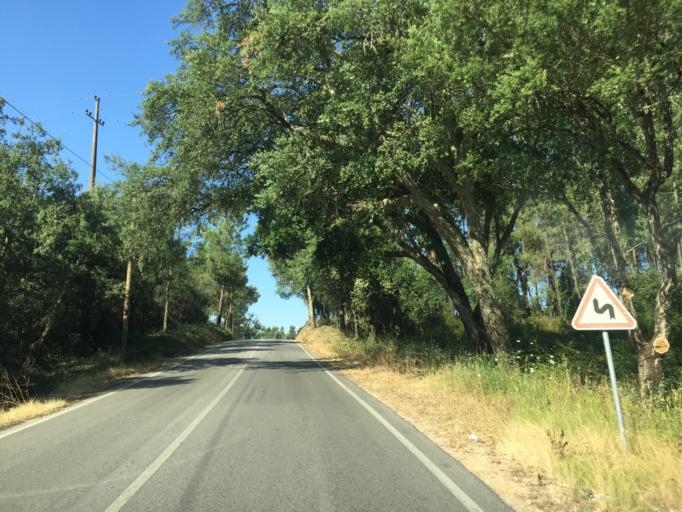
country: PT
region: Santarem
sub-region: Ferreira do Zezere
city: Ferreira do Zezere
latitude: 39.6030
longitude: -8.3121
